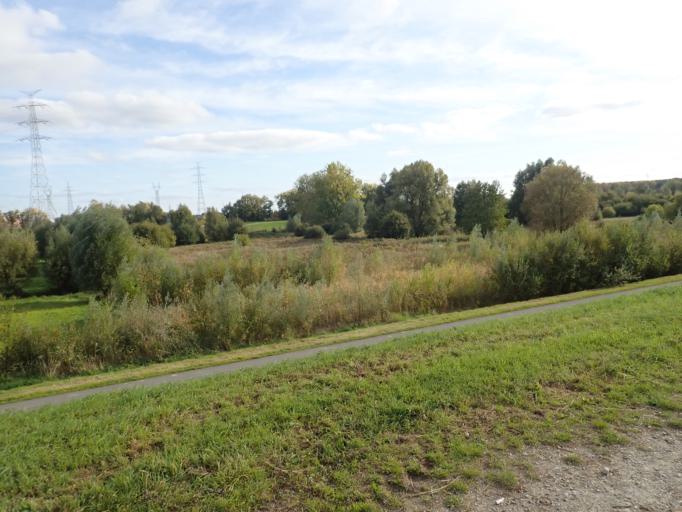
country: BE
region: Flanders
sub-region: Provincie Antwerpen
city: Niel
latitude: 51.1292
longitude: 4.2988
